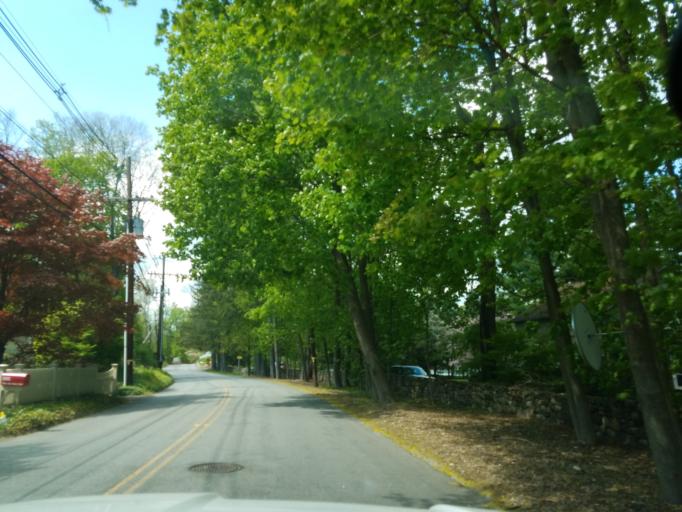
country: US
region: Connecticut
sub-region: Fairfield County
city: New Canaan
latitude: 41.1302
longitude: -73.4764
